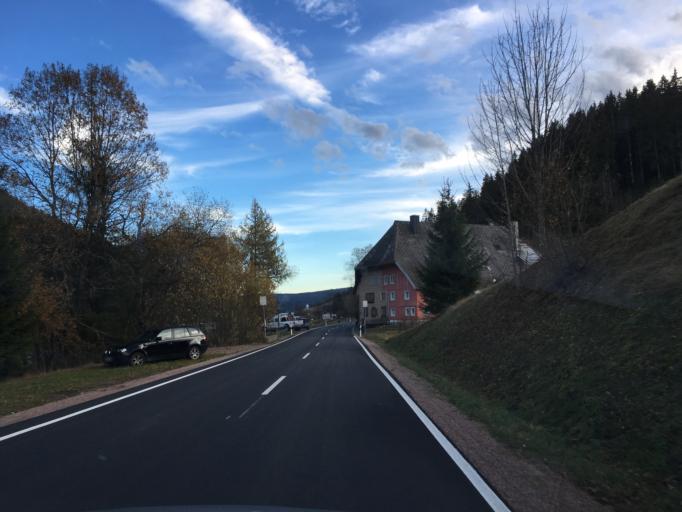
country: DE
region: Baden-Wuerttemberg
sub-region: Freiburg Region
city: Furtwangen im Schwarzwald
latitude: 48.0750
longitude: 8.1861
